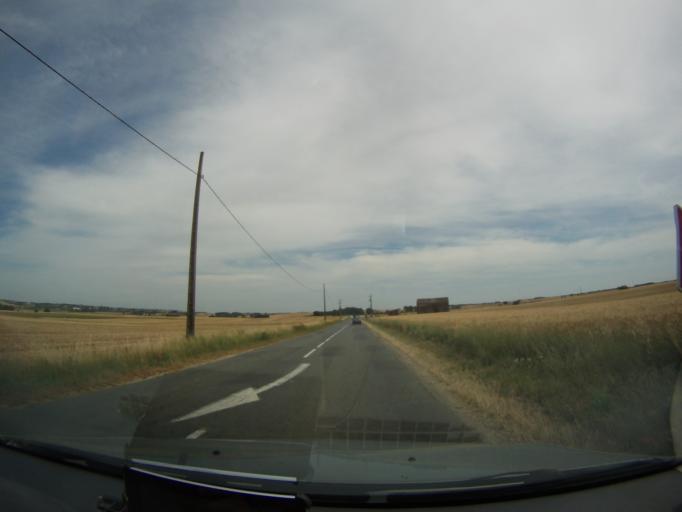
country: FR
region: Poitou-Charentes
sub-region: Departement de la Vienne
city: Mirebeau
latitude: 46.7867
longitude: 0.1249
